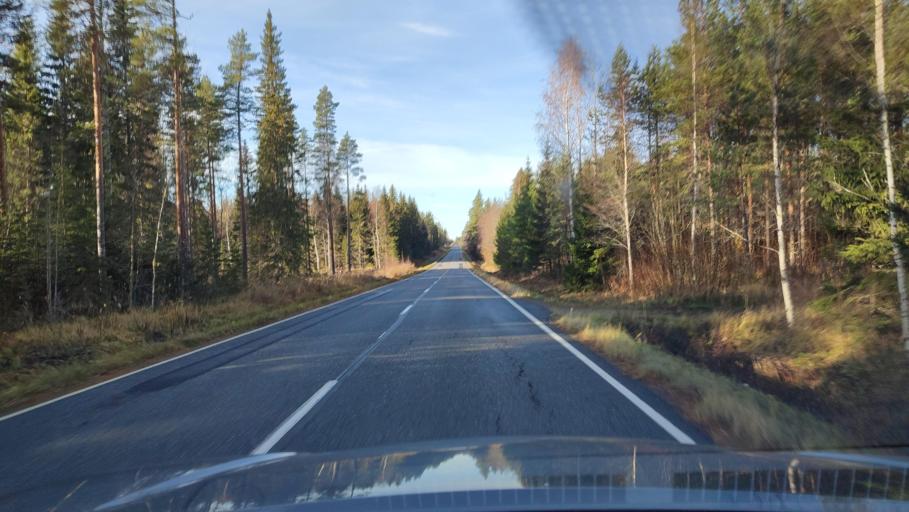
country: FI
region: Southern Ostrobothnia
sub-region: Suupohja
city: Teuva
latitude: 62.4604
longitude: 21.5466
